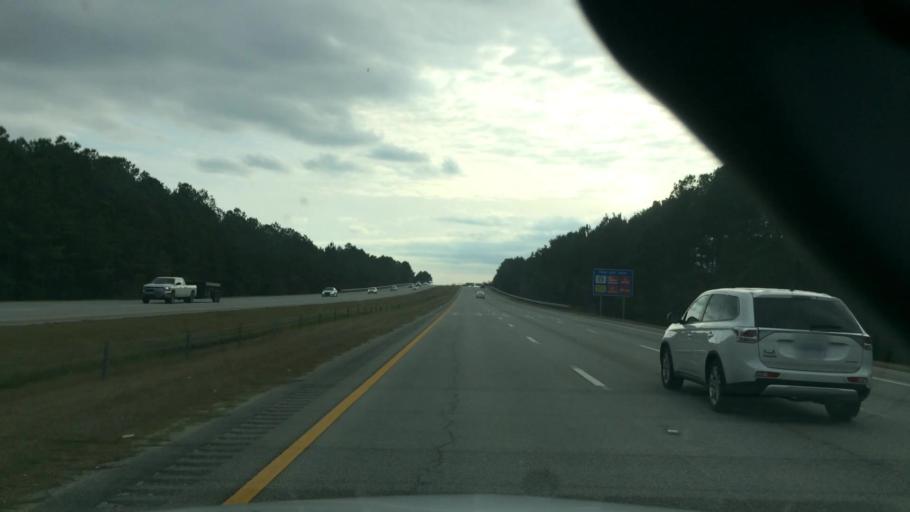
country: US
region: South Carolina
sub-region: Horry County
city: North Myrtle Beach
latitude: 33.8575
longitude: -78.6966
